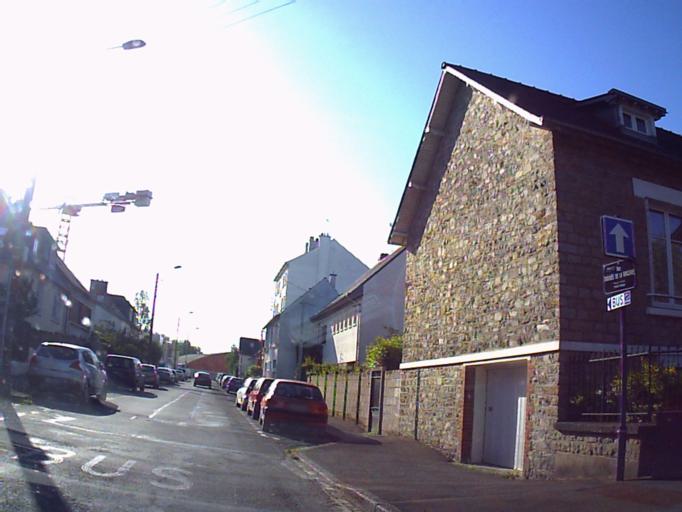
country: FR
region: Brittany
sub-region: Departement d'Ille-et-Vilaine
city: Rennes
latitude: 48.1239
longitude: -1.6533
